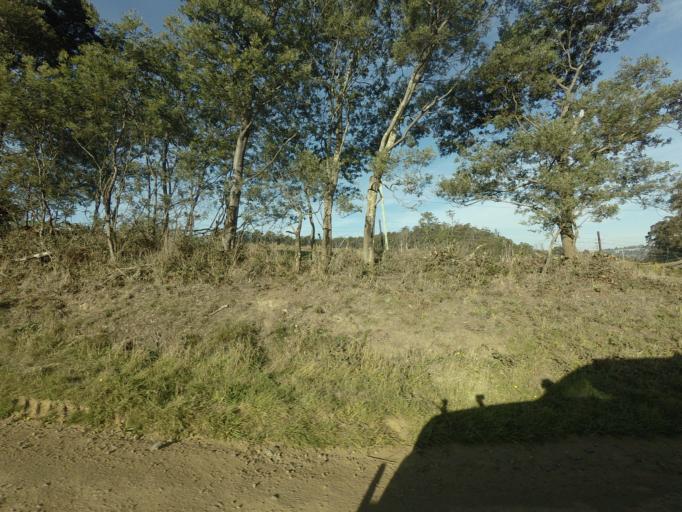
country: AU
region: Tasmania
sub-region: Brighton
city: Bridgewater
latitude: -42.4631
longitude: 147.3769
